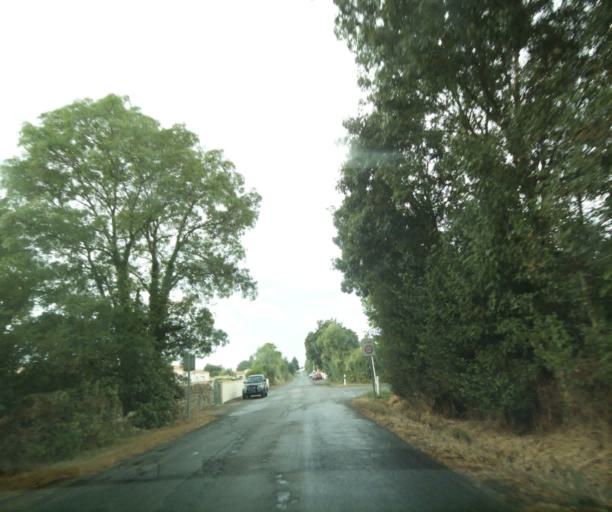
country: FR
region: Poitou-Charentes
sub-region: Departement de la Charente-Maritime
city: Tonnay-Charente
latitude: 45.9423
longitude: -0.8774
